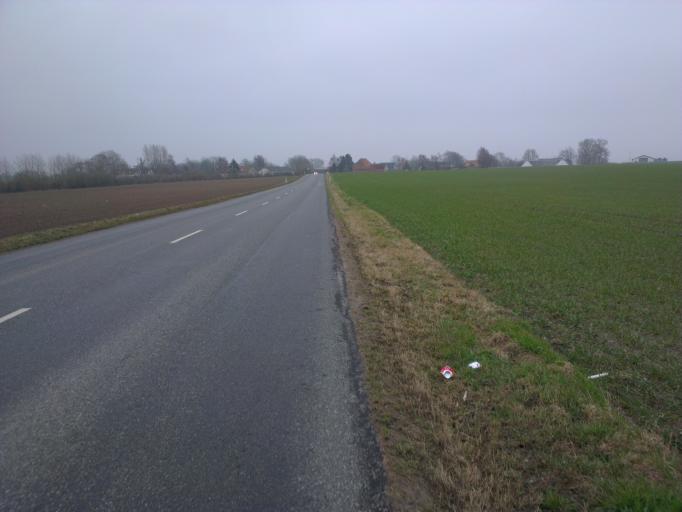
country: DK
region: Capital Region
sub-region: Frederikssund Kommune
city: Frederikssund
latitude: 55.8140
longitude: 12.0193
